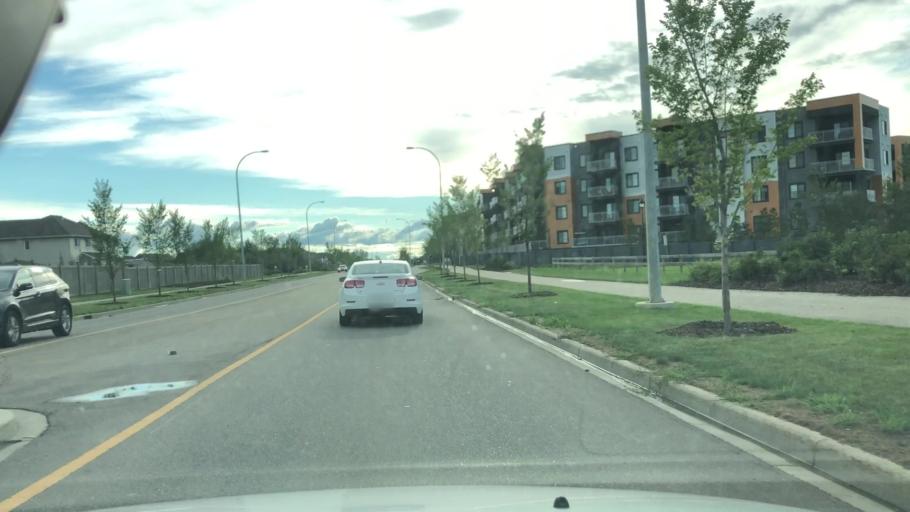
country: CA
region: Alberta
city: St. Albert
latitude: 53.6287
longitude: -113.5526
